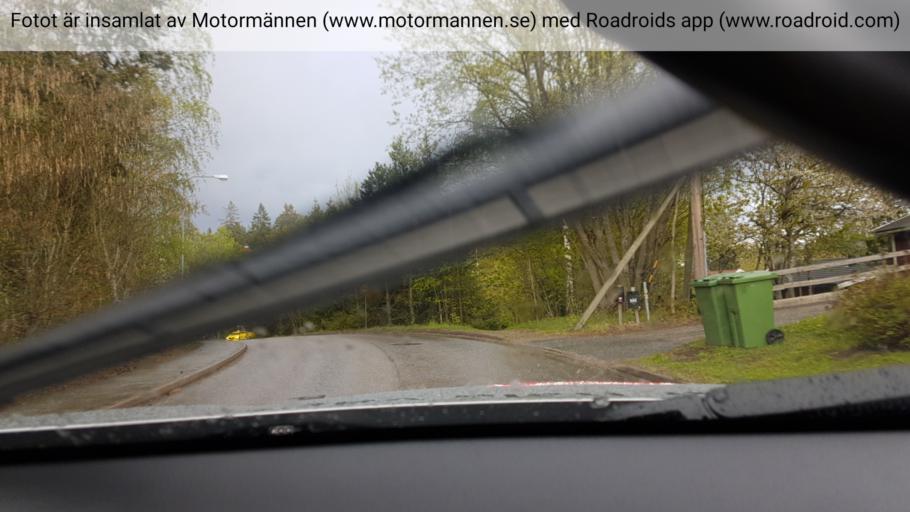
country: SE
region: Stockholm
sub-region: Huddinge Kommun
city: Huddinge
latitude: 59.2288
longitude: 17.9763
